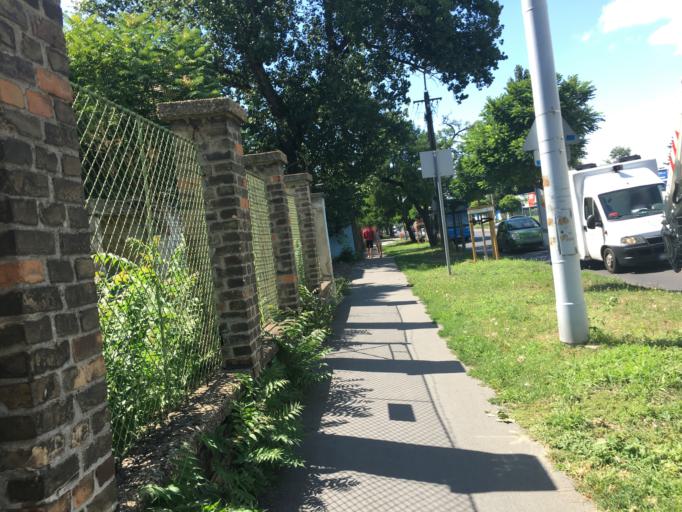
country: HU
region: Budapest
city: Budapest X. keruelet
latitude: 47.4669
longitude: 19.1532
